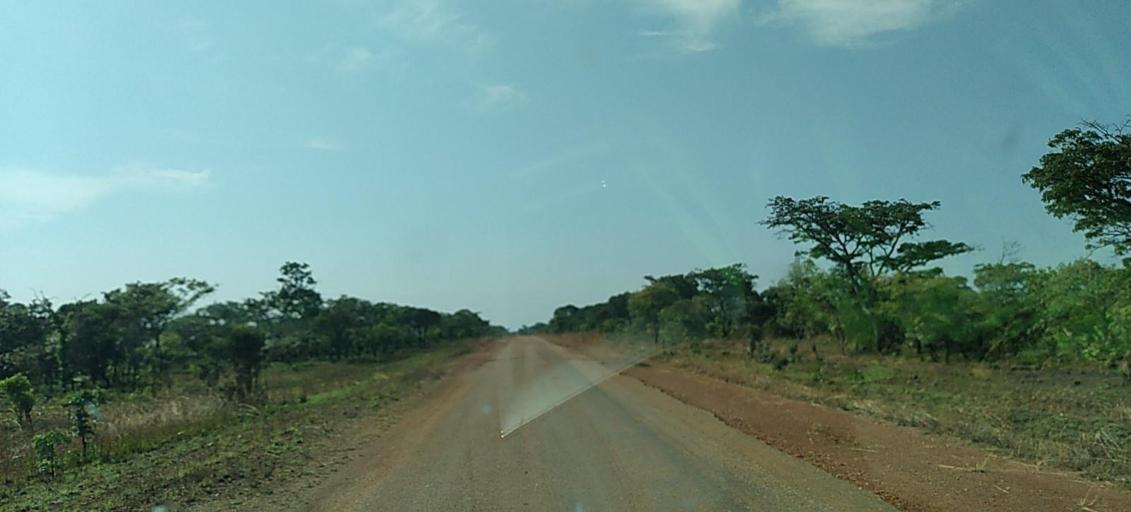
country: ZM
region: North-Western
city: Mwinilunga
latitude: -11.7947
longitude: 25.0724
